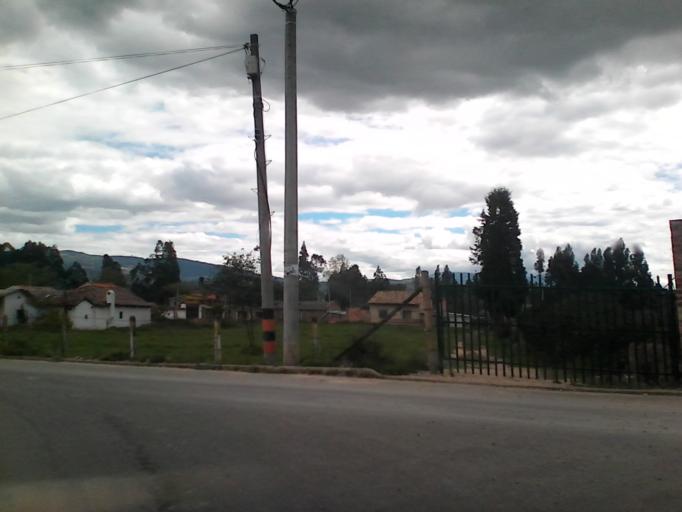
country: CO
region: Boyaca
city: Duitama
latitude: 5.8144
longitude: -73.0722
